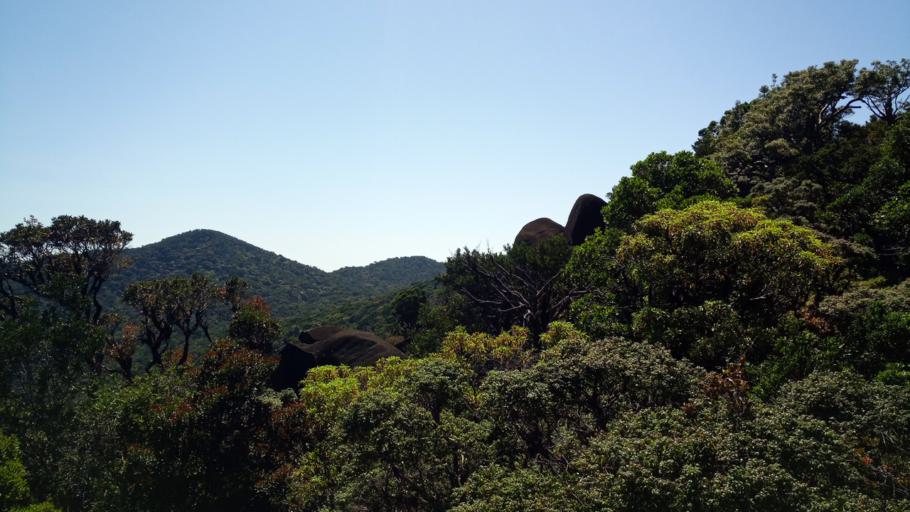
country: AU
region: Queensland
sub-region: Cassowary Coast
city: Innisfail
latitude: -17.3851
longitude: 145.8018
